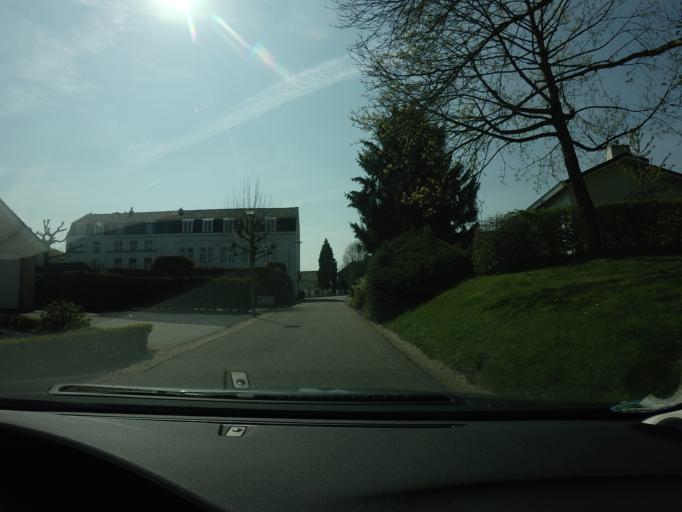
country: NL
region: Limburg
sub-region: Valkenburg aan de Geul
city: Berg
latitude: 50.8457
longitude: 5.7638
